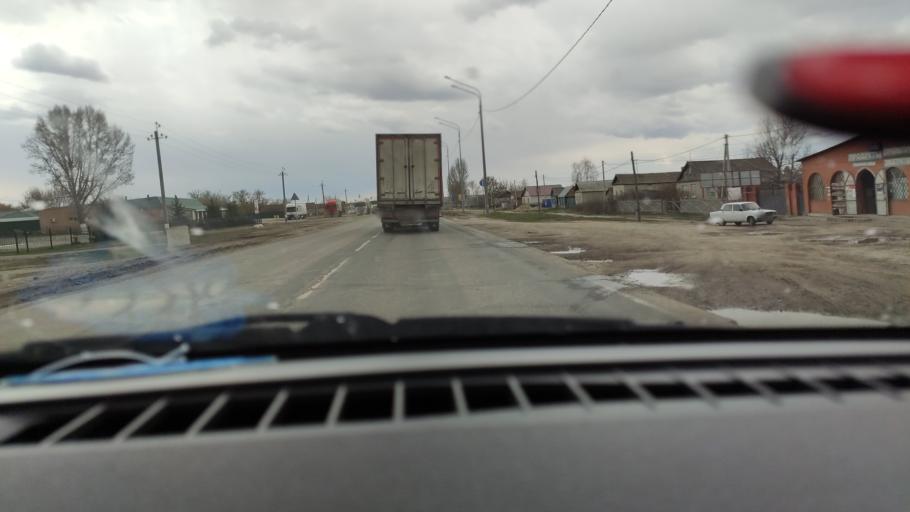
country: RU
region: Saratov
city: Sinodskoye
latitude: 51.9840
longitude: 46.6617
